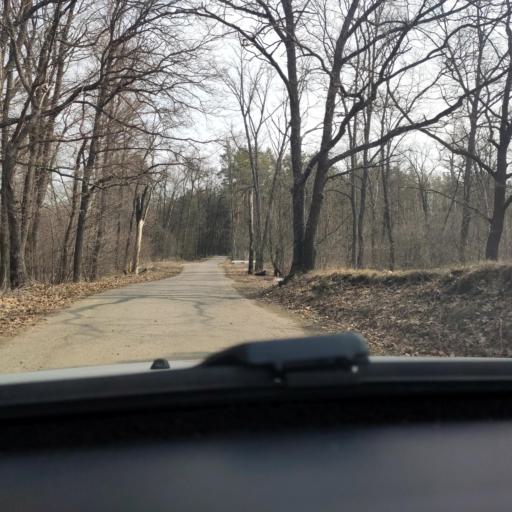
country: RU
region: Voronezj
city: Ramon'
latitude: 51.8898
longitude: 39.3613
